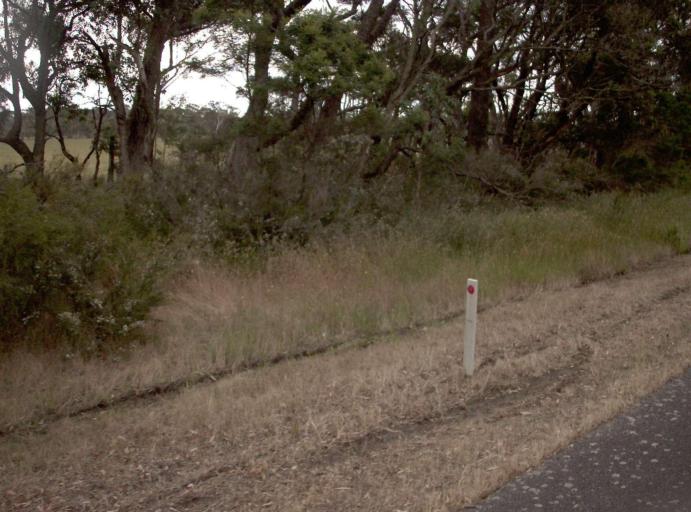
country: AU
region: Victoria
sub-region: Wellington
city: Sale
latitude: -38.4758
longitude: 146.9247
